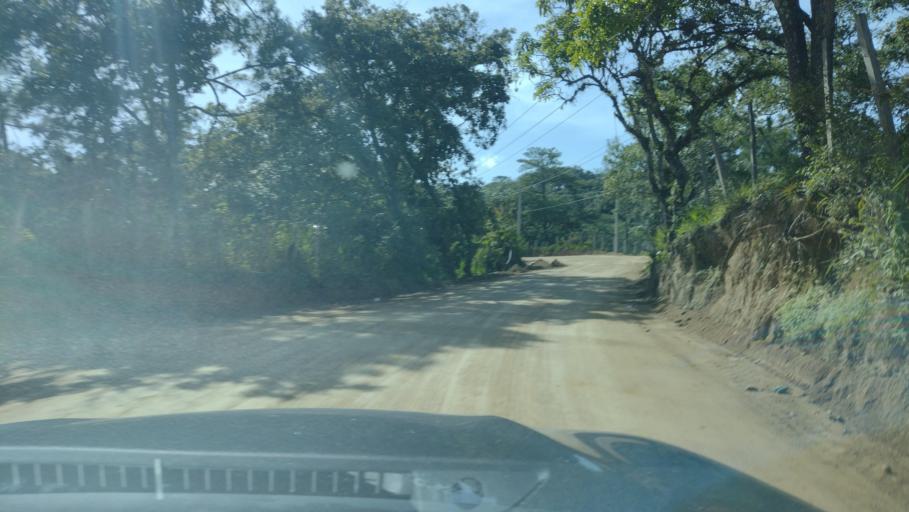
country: GT
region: Guatemala
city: Chinautla
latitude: 14.7616
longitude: -90.5244
